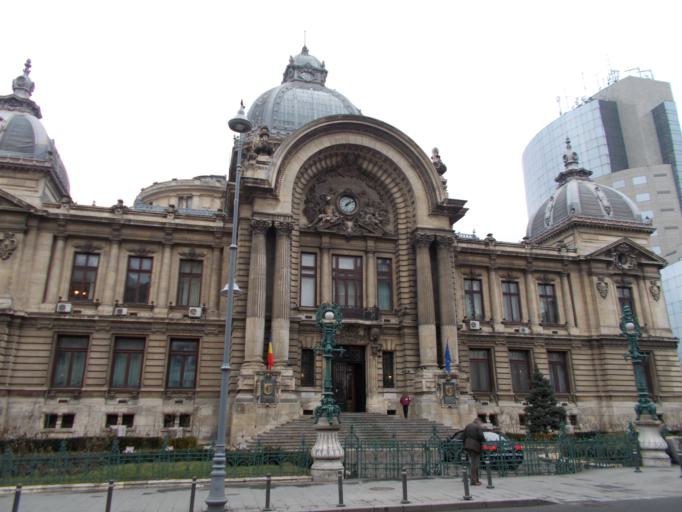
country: RO
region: Bucuresti
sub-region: Municipiul Bucuresti
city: Bucuresti
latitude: 44.4321
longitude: 26.0972
